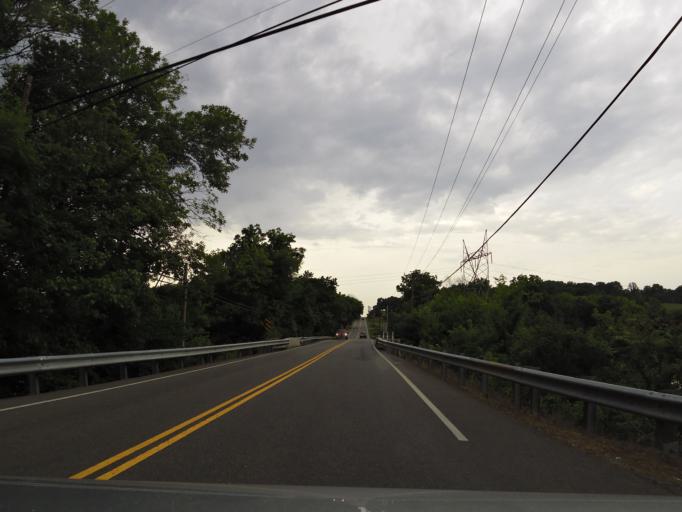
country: US
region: Tennessee
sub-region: Blount County
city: Eagleton Village
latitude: 35.8473
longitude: -83.9408
